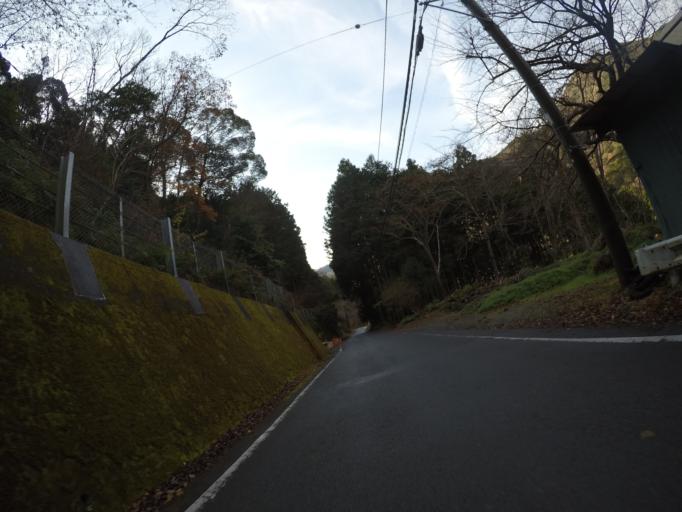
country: JP
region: Shizuoka
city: Heda
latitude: 34.8188
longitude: 138.8320
